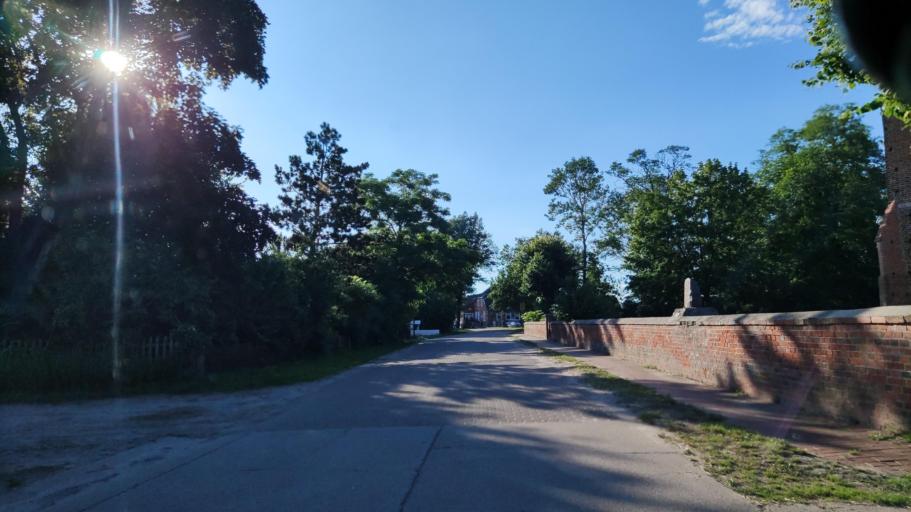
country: DE
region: Lower Saxony
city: Gartow
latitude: 53.0320
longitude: 11.5104
